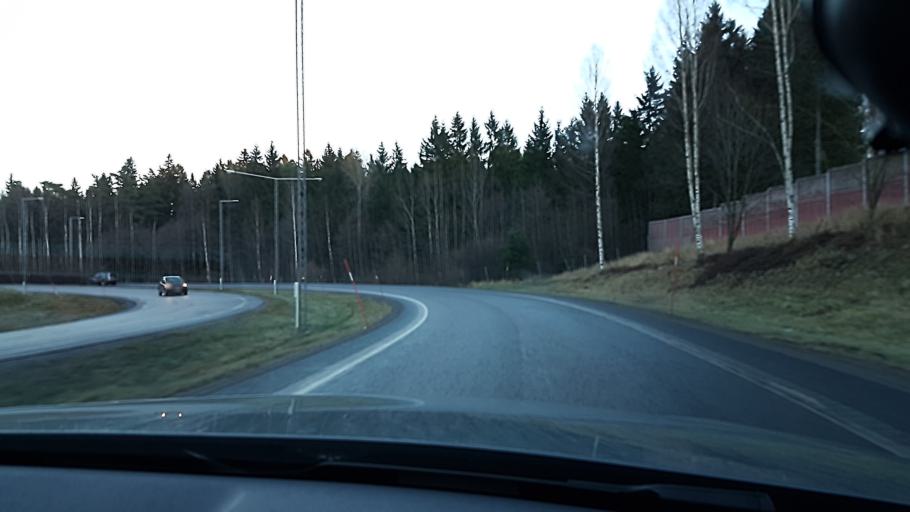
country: SE
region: Stockholm
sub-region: Sodertalje Kommun
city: Pershagen
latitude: 59.1580
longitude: 17.6475
